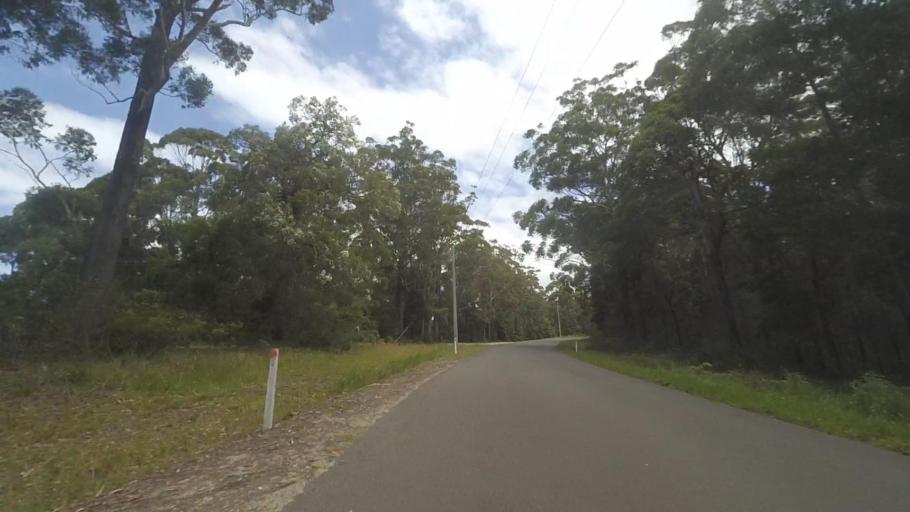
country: AU
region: New South Wales
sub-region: Shoalhaven Shire
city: Milton
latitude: -35.3816
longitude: 150.3719
